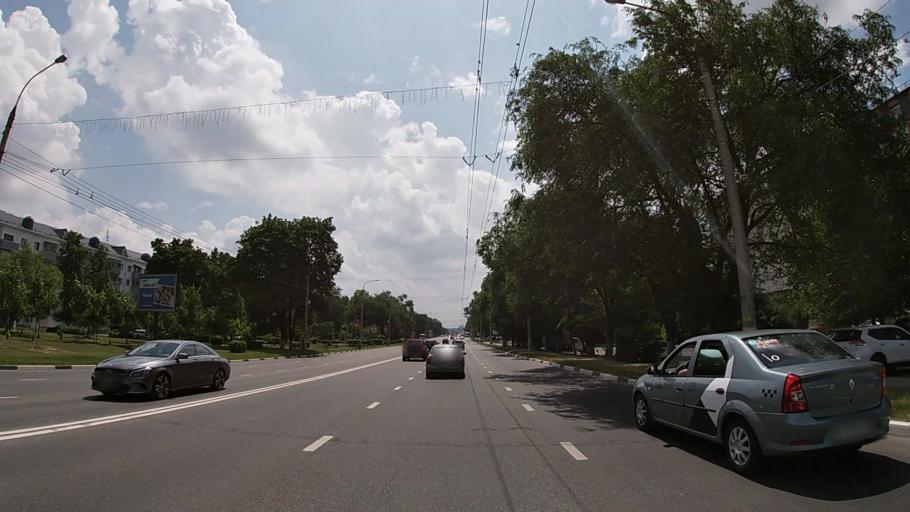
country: RU
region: Belgorod
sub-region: Belgorodskiy Rayon
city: Belgorod
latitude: 50.6157
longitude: 36.5776
